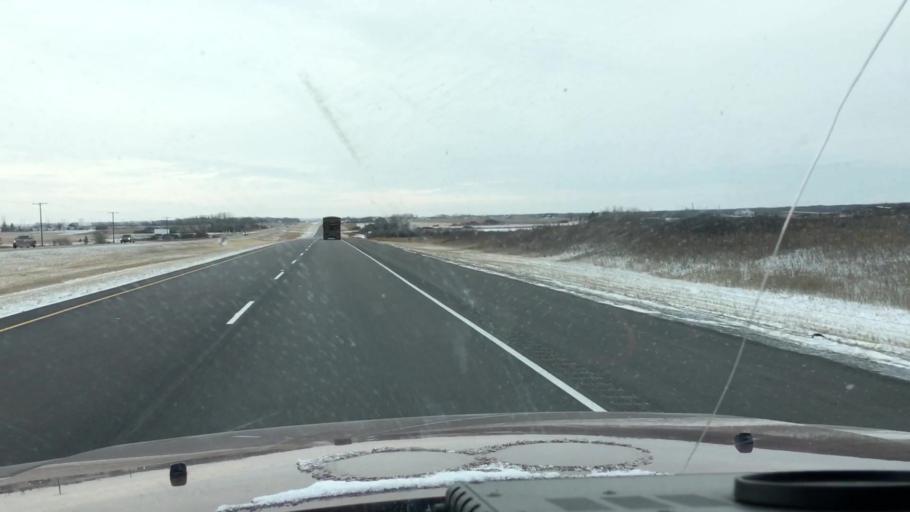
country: CA
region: Saskatchewan
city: Saskatoon
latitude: 51.9265
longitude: -106.5337
